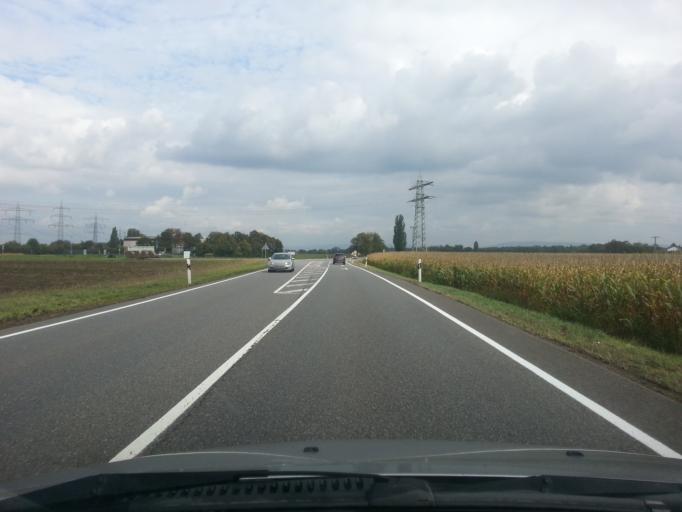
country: DE
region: Baden-Wuerttemberg
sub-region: Karlsruhe Region
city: Ketsch
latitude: 49.3358
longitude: 8.5161
